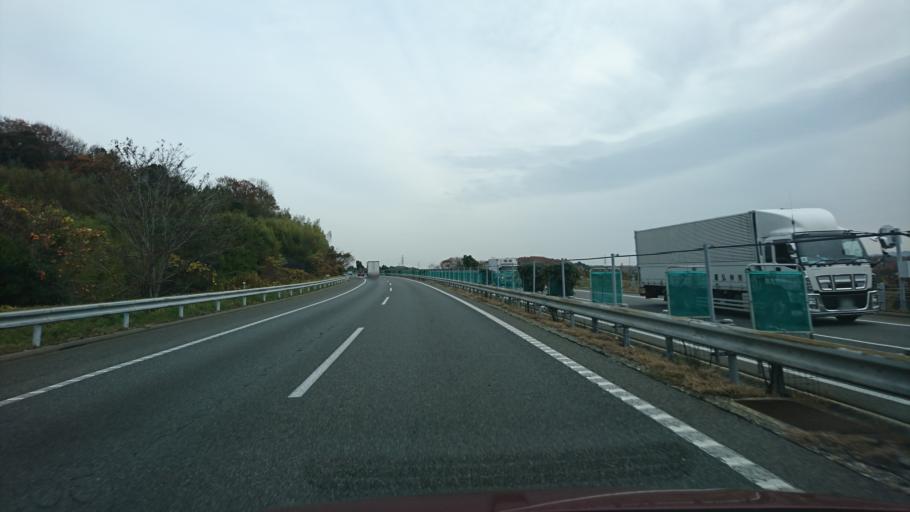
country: JP
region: Hyogo
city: Sandacho
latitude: 34.8216
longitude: 135.1423
